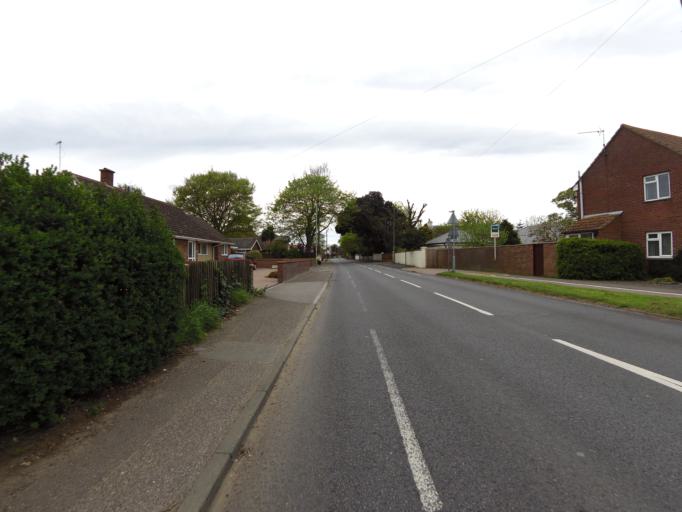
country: GB
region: England
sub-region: Suffolk
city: Felixstowe
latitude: 51.9812
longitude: 1.3173
